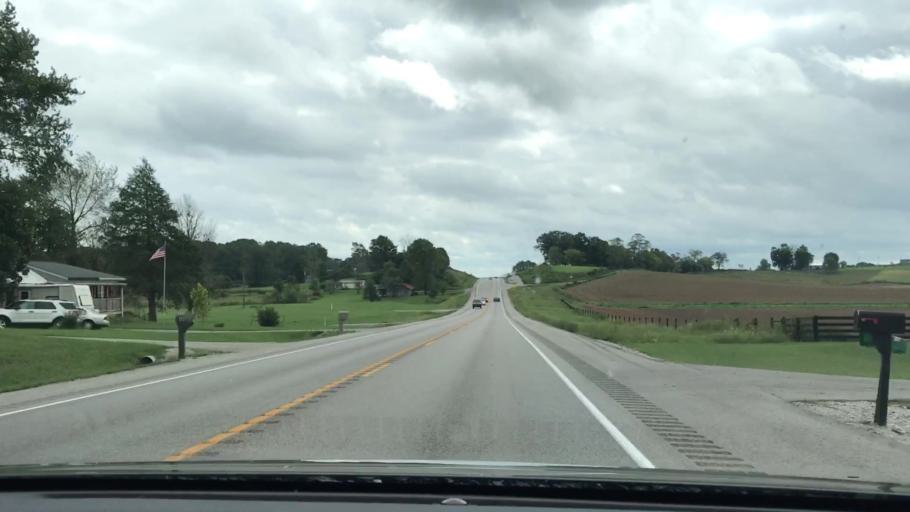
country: US
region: Kentucky
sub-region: Barren County
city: Glasgow
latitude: 36.9522
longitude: -85.8517
